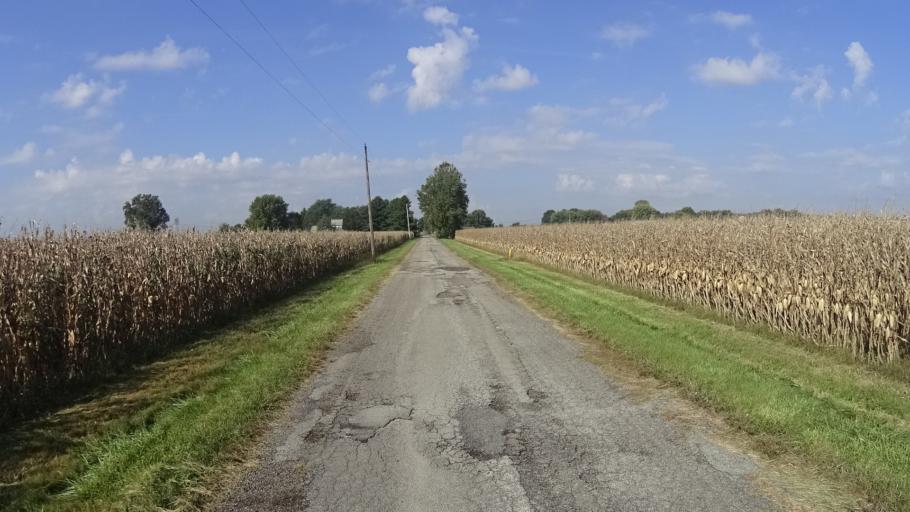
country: US
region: Indiana
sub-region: Madison County
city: Lapel
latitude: 40.0315
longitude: -85.8381
